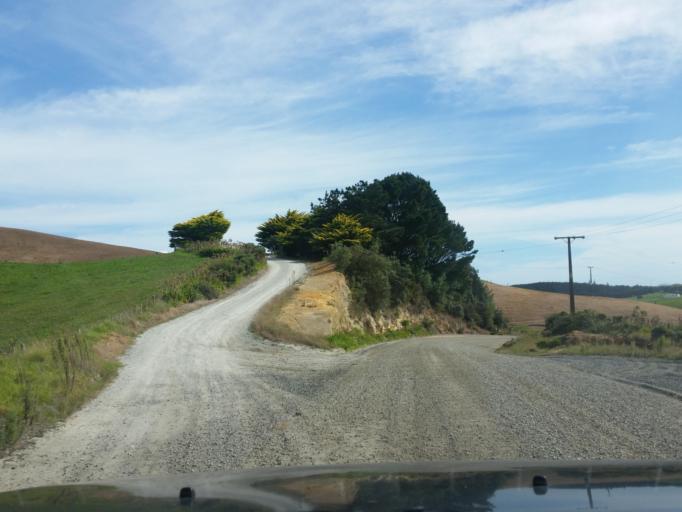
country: NZ
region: Northland
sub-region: Kaipara District
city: Dargaville
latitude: -35.9261
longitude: 173.7385
